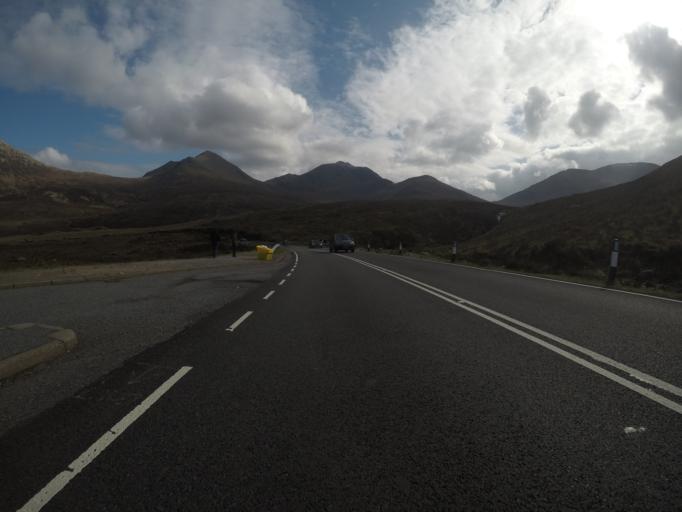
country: GB
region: Scotland
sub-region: Highland
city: Portree
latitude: 57.2643
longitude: -6.0910
